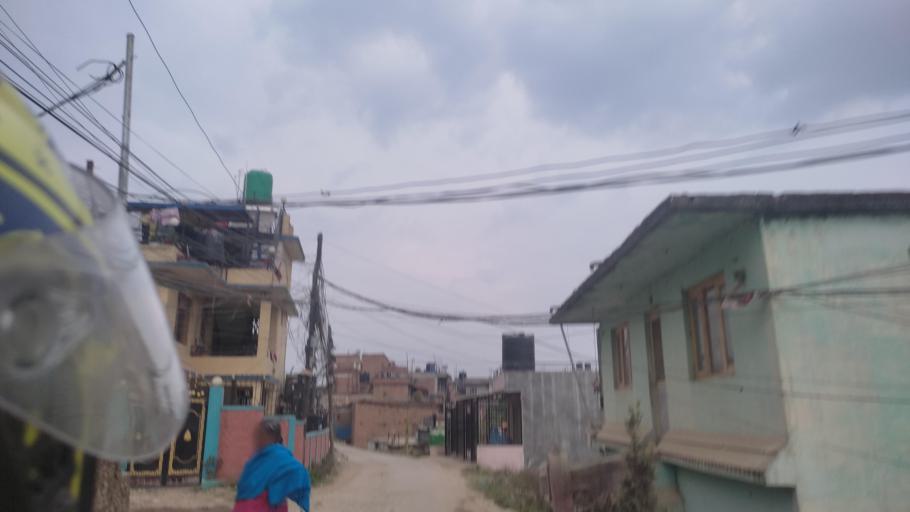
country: NP
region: Central Region
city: Kirtipur
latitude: 27.6672
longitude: 85.2726
